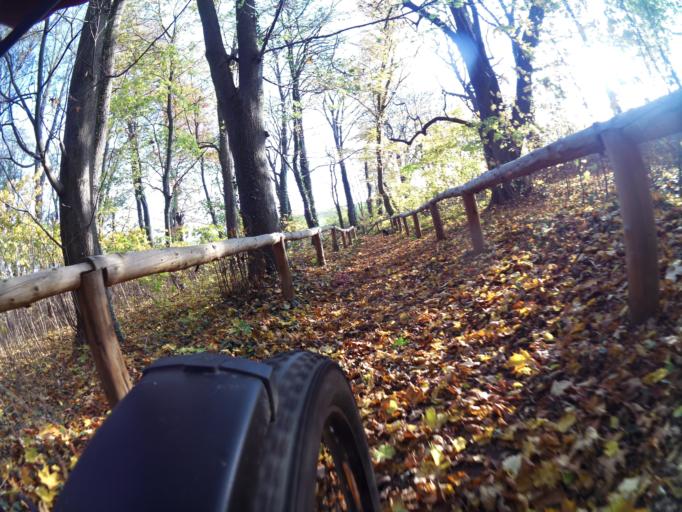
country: PL
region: Pomeranian Voivodeship
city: Strzelno
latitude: 54.7574
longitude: 18.2911
